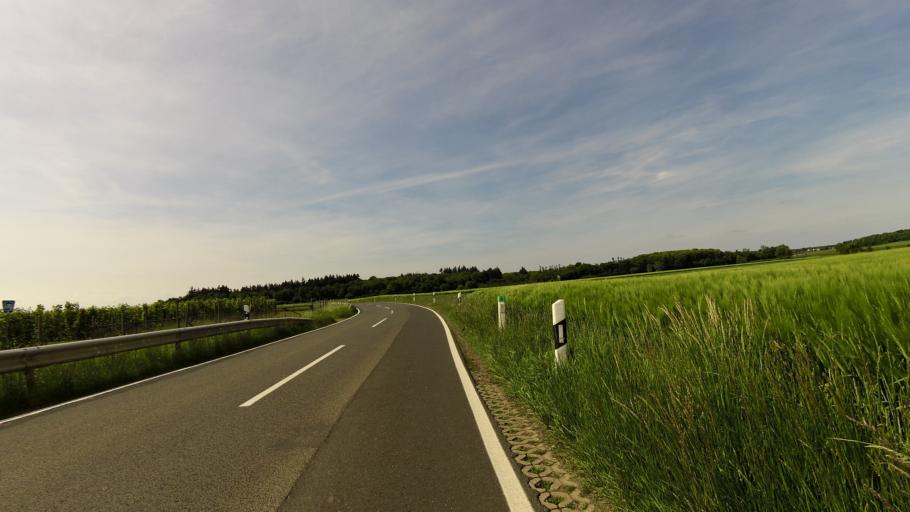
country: DE
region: North Rhine-Westphalia
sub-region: Regierungsbezirk Koln
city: Rheinbach
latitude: 50.6622
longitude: 6.9750
